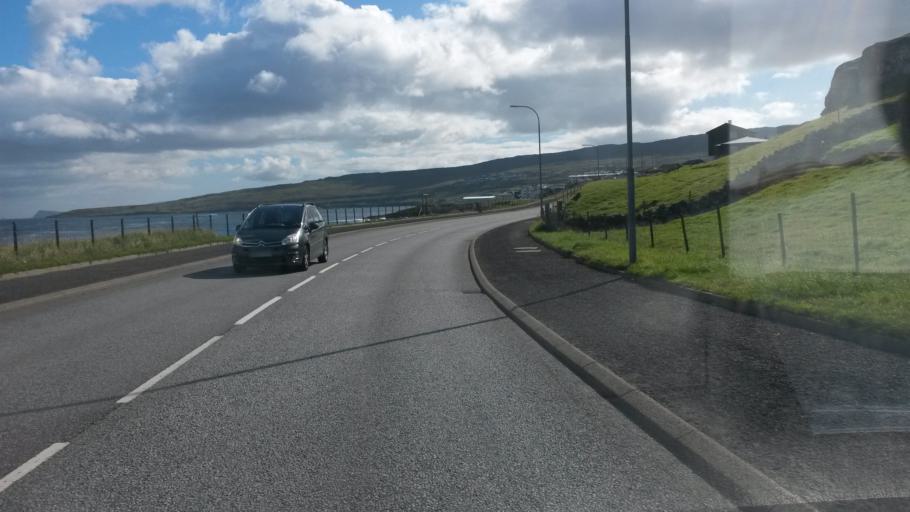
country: FO
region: Streymoy
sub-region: Torshavn
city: Torshavn
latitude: 62.0156
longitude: -6.7555
